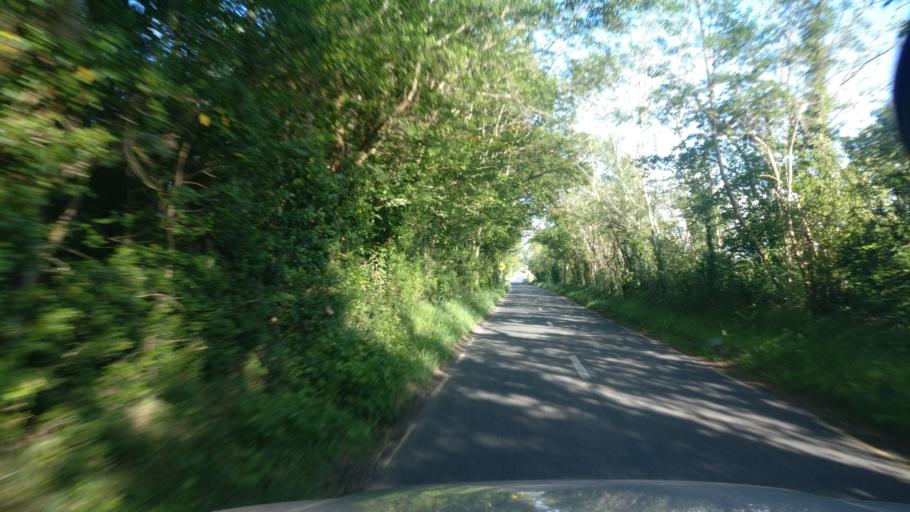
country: IE
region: Connaught
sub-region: County Galway
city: Ballinasloe
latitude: 53.2222
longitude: -8.1968
